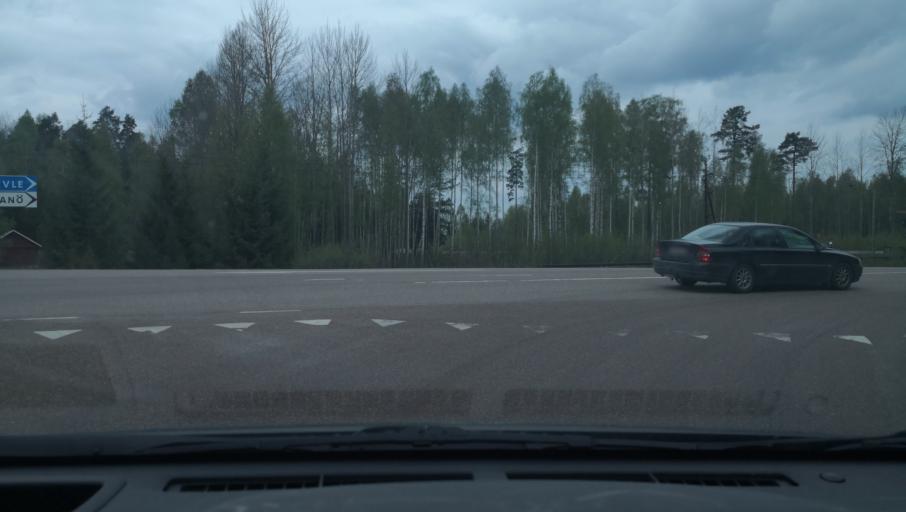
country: SE
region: Dalarna
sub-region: Avesta Kommun
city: Avesta
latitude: 60.1463
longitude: 16.2298
